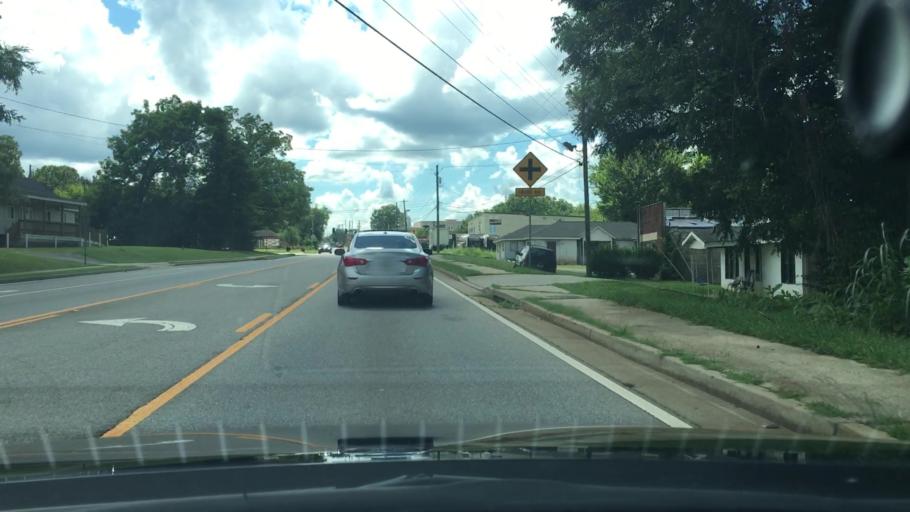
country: US
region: Georgia
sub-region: Putnam County
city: Eatonton
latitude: 33.3276
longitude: -83.3819
